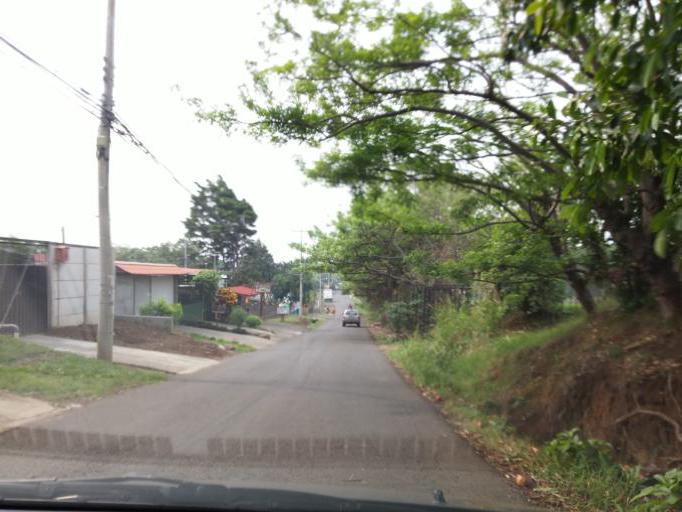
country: CR
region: Alajuela
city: Alajuela
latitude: 9.9856
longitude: -84.2261
